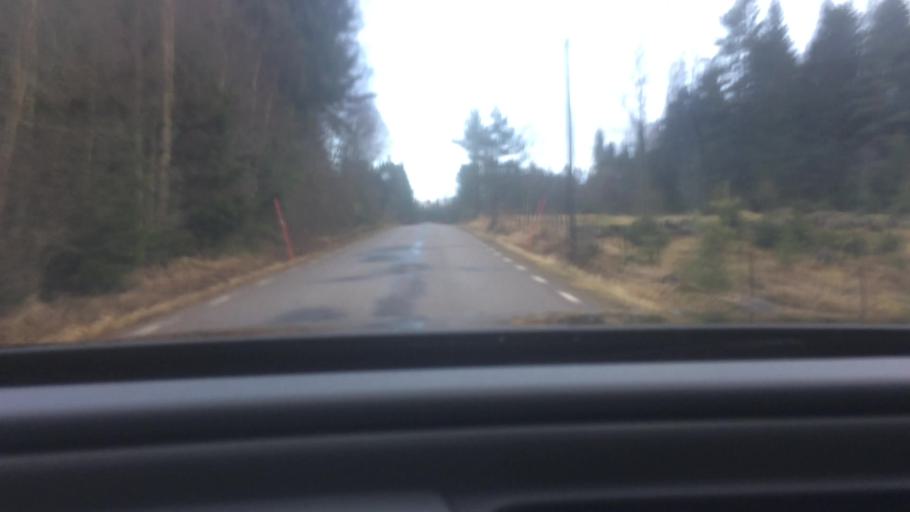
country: SE
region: Vaestra Goetaland
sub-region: Falkopings Kommun
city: Falkoeping
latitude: 57.9958
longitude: 13.4762
